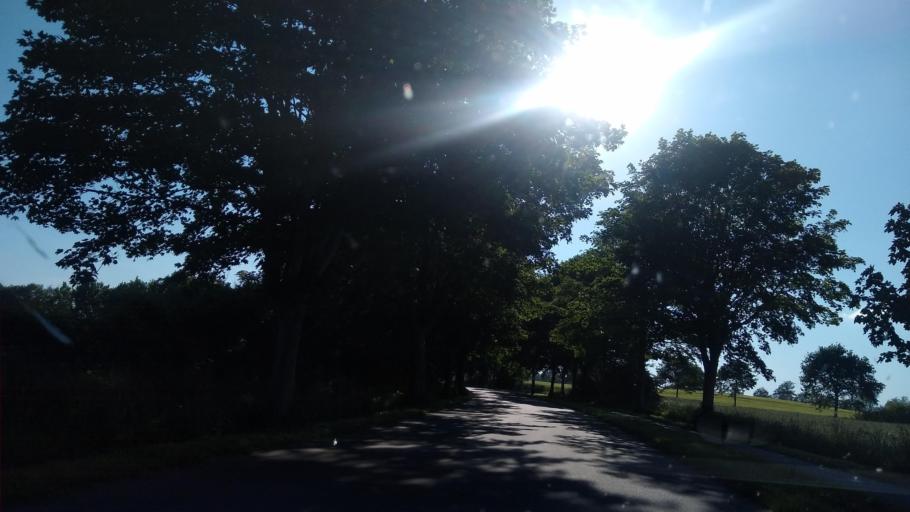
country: DE
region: Schleswig-Holstein
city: Neudorf-Bornstein
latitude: 54.4119
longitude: 9.9571
